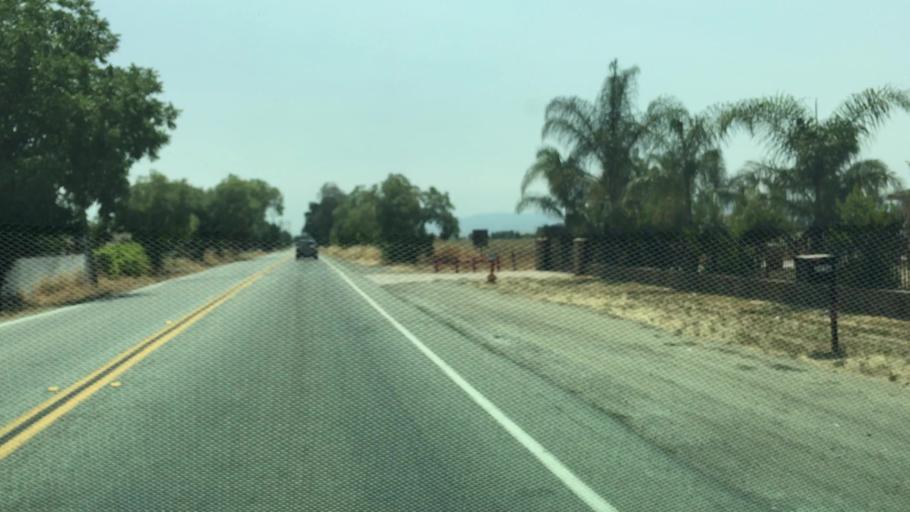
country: US
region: California
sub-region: Santa Clara County
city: Gilroy
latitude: 37.0152
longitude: -121.5190
